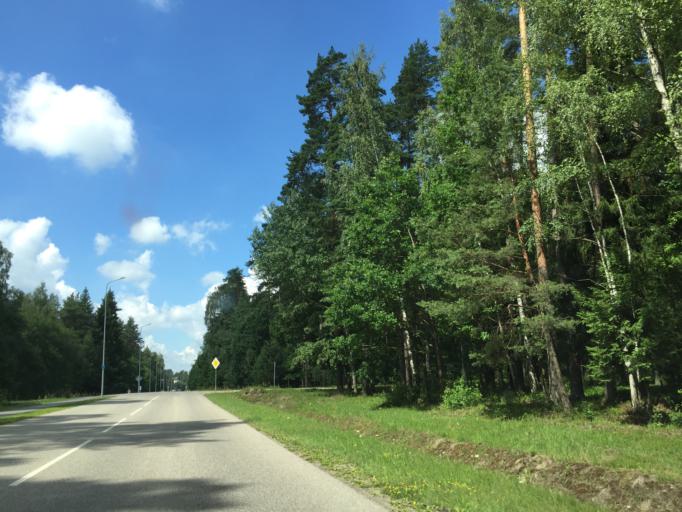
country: LV
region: Ozolnieku
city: Ozolnieki
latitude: 56.6927
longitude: 23.7787
